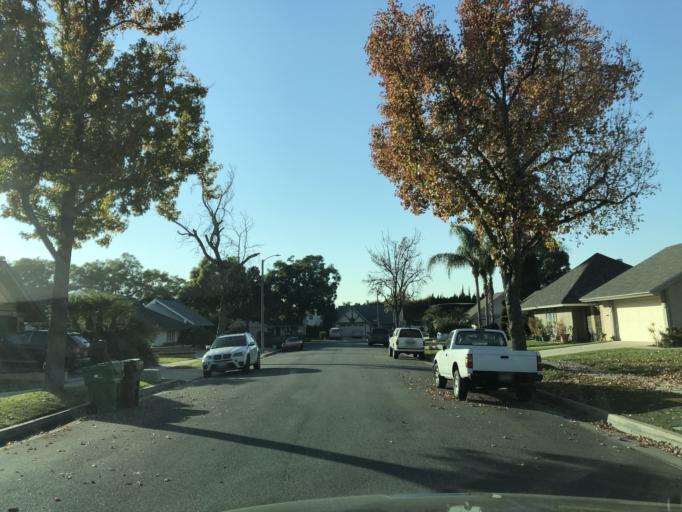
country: US
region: California
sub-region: Orange County
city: Orange
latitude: 33.7691
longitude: -117.8463
